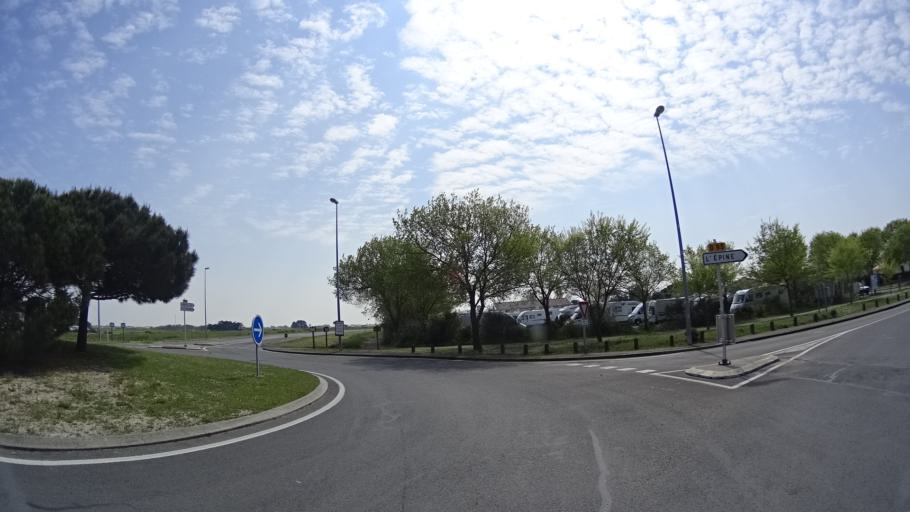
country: FR
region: Pays de la Loire
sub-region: Departement de la Vendee
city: La Gueriniere
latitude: 46.9819
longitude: -2.2638
